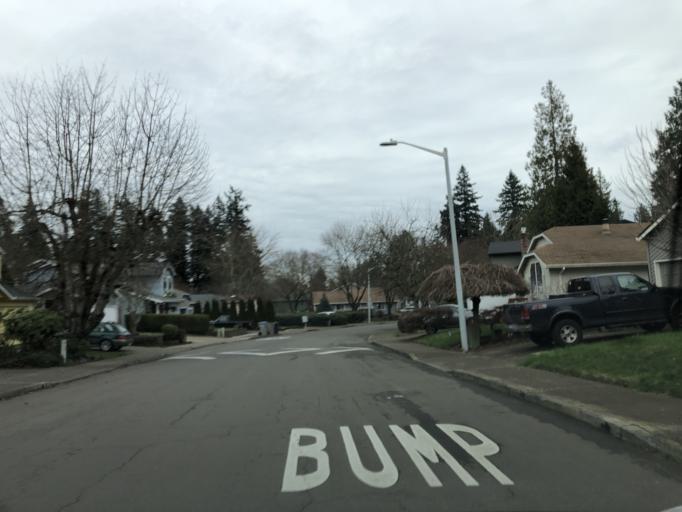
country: US
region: Oregon
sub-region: Washington County
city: Tigard
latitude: 45.4174
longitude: -122.7631
